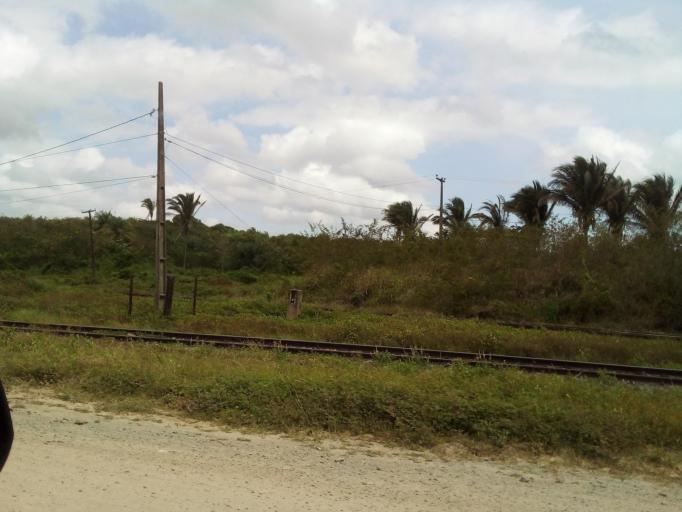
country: BR
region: Maranhao
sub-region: Icatu
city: Icatu
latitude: -2.9271
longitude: -44.3460
